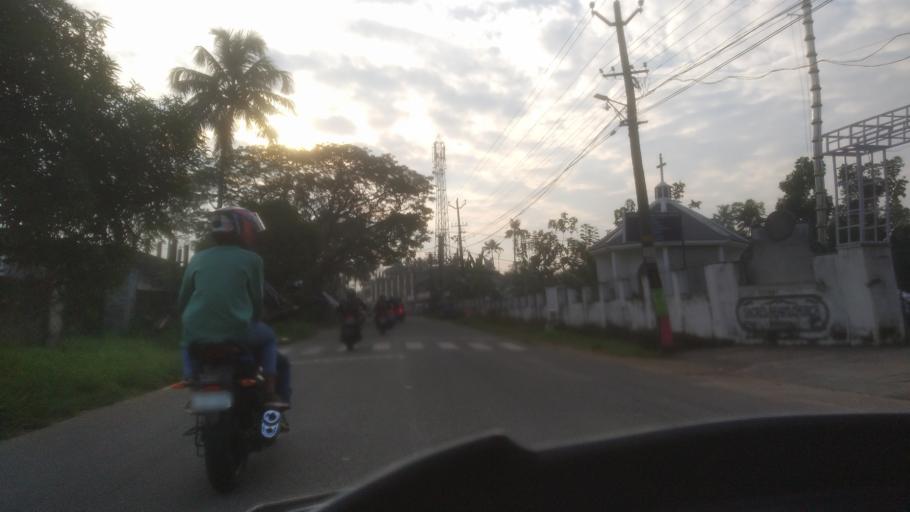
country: IN
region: Kerala
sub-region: Ernakulam
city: Perumpavur
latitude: 10.1180
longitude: 76.4422
